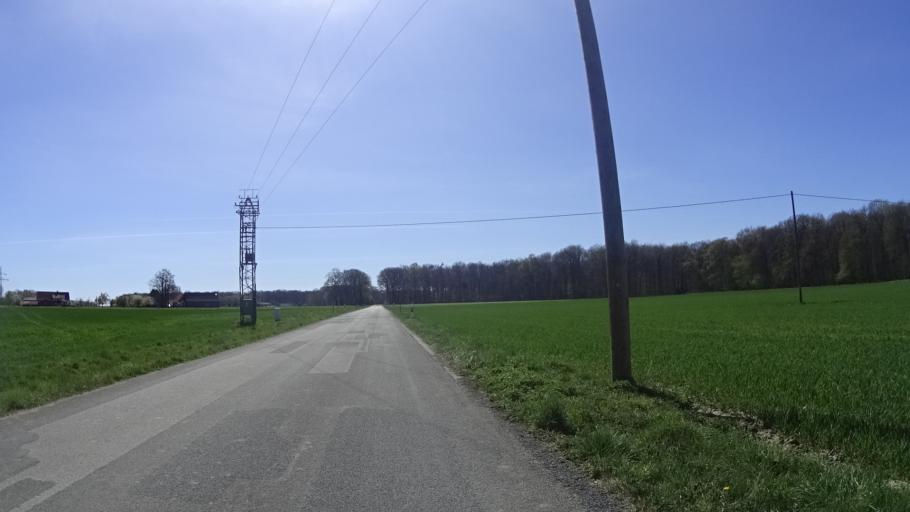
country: DE
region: North Rhine-Westphalia
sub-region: Regierungsbezirk Munster
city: Dulmen
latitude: 51.8147
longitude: 7.3497
